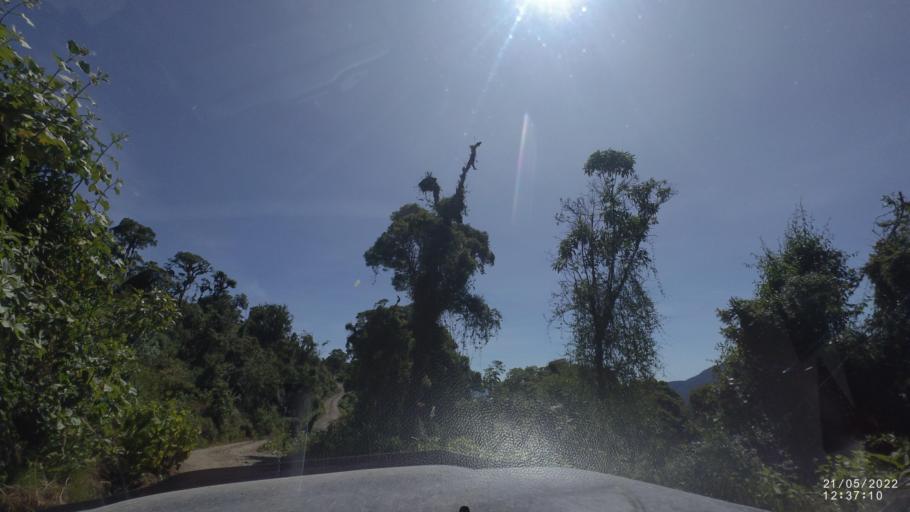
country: BO
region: Cochabamba
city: Colomi
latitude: -17.2023
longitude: -65.9196
